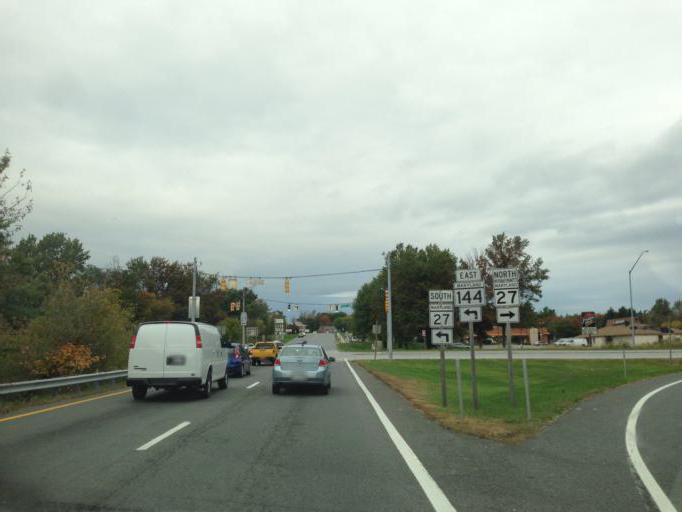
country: US
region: Maryland
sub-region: Carroll County
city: Mount Airy
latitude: 39.3615
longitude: -77.1632
